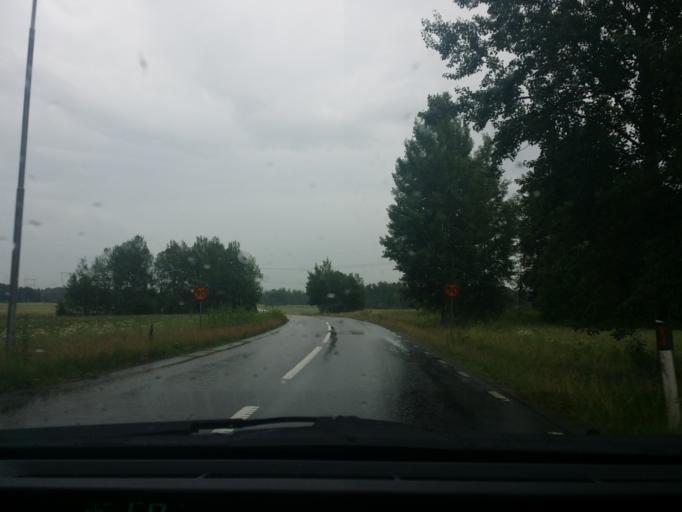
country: SE
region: OErebro
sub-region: Lindesbergs Kommun
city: Fellingsbro
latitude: 59.4273
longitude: 15.6017
